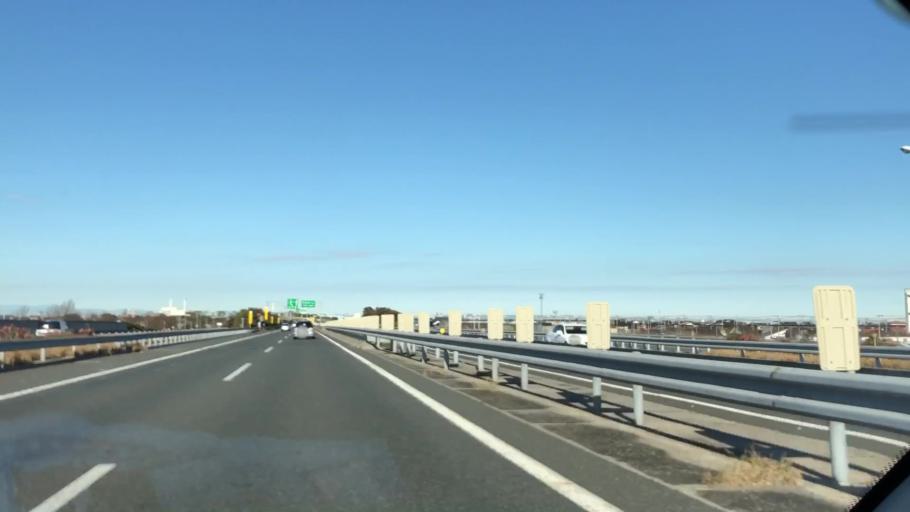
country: JP
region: Chiba
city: Kisarazu
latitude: 35.4283
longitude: 139.9282
